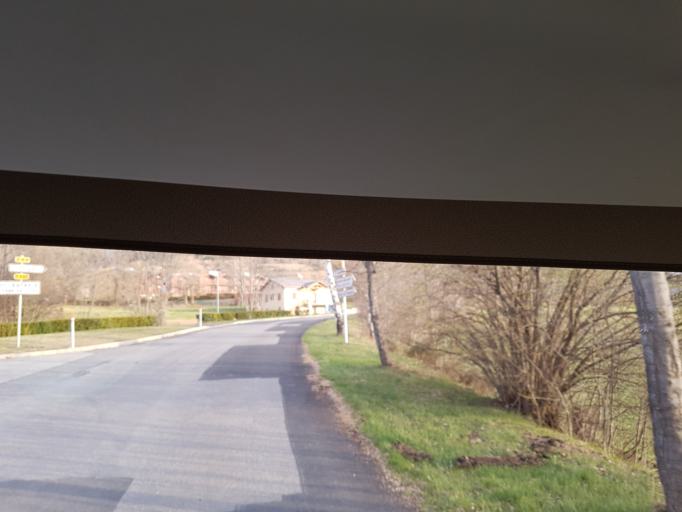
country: FR
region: Languedoc-Roussillon
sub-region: Departement des Pyrenees-Orientales
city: Osseja
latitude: 42.4381
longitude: 2.0168
